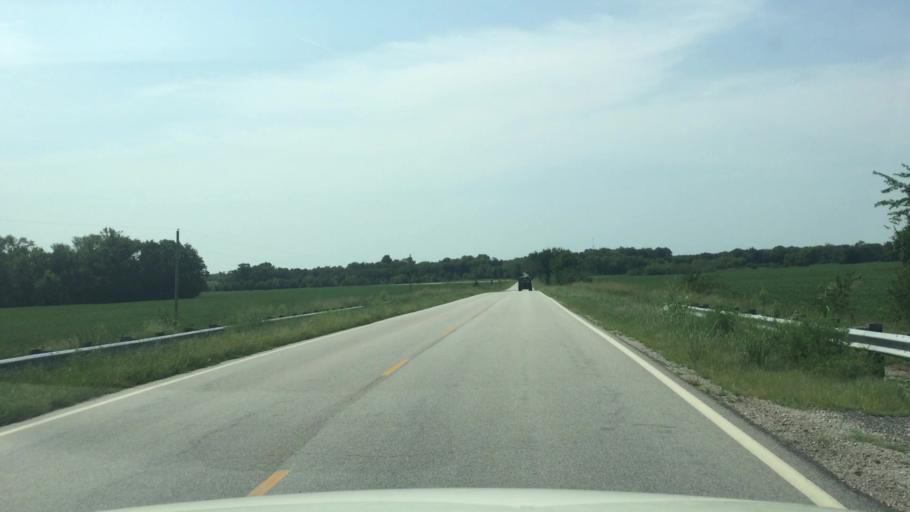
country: US
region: Kansas
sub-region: Montgomery County
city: Cherryvale
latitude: 37.1997
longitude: -95.5579
